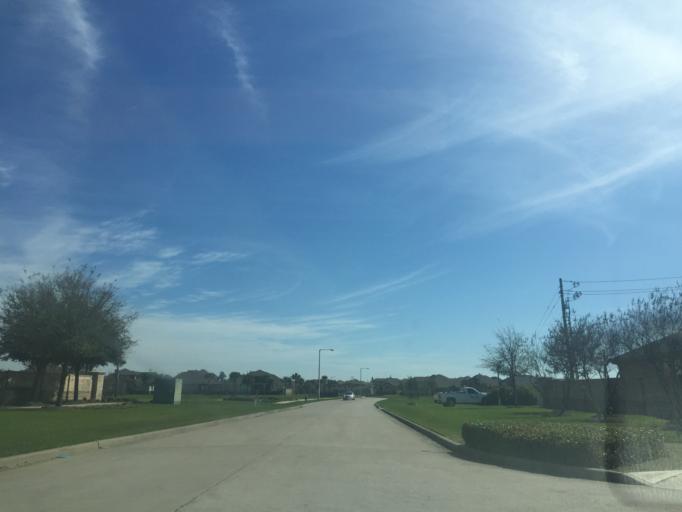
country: US
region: Texas
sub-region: Galveston County
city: Bacliff
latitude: 29.5114
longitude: -95.0169
